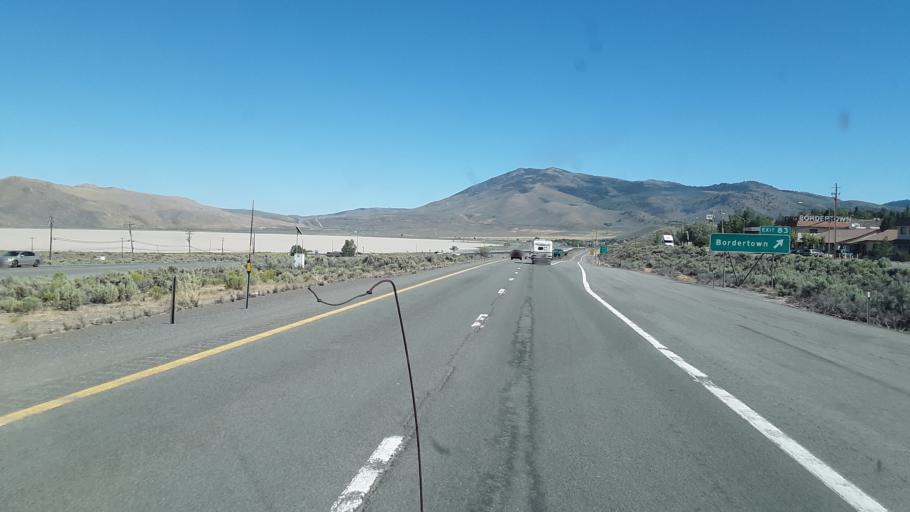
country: US
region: Nevada
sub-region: Washoe County
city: Cold Springs
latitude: 39.6727
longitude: -120.0006
